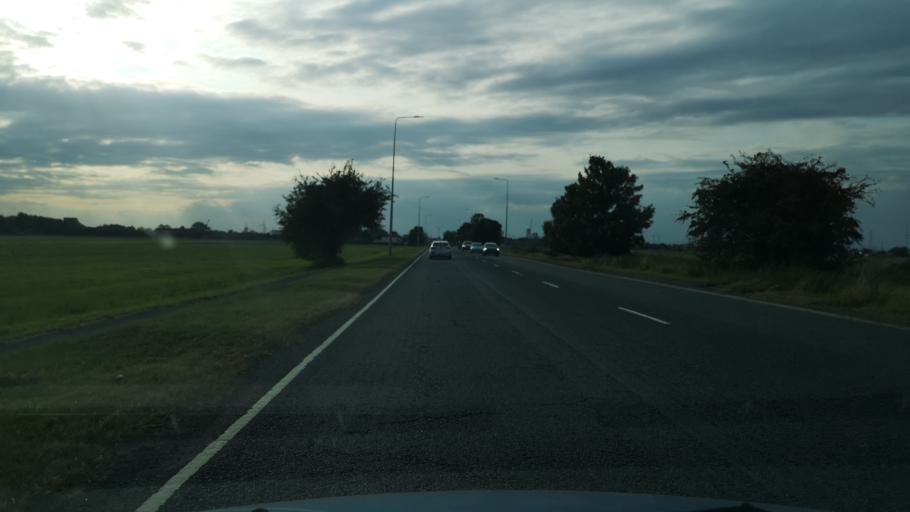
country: GB
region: England
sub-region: North Lincolnshire
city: Gunness
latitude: 53.5896
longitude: -0.7138
